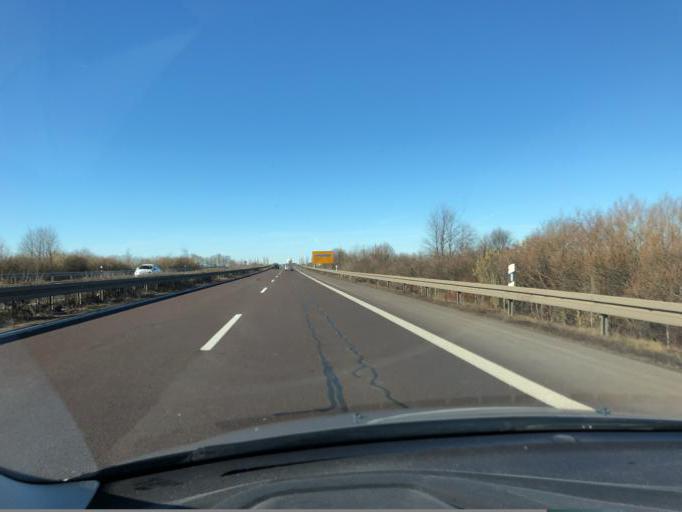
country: DE
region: Saxony-Anhalt
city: Frose
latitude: 51.7744
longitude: 11.3962
